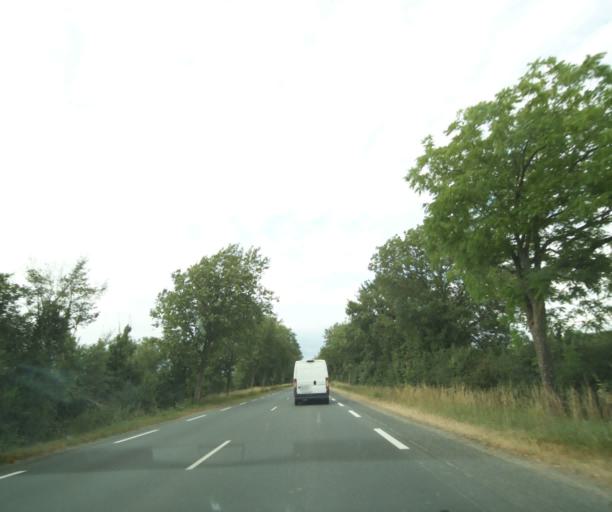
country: FR
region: Poitou-Charentes
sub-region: Departement de la Charente-Maritime
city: Andilly
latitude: 46.2735
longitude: -1.0017
